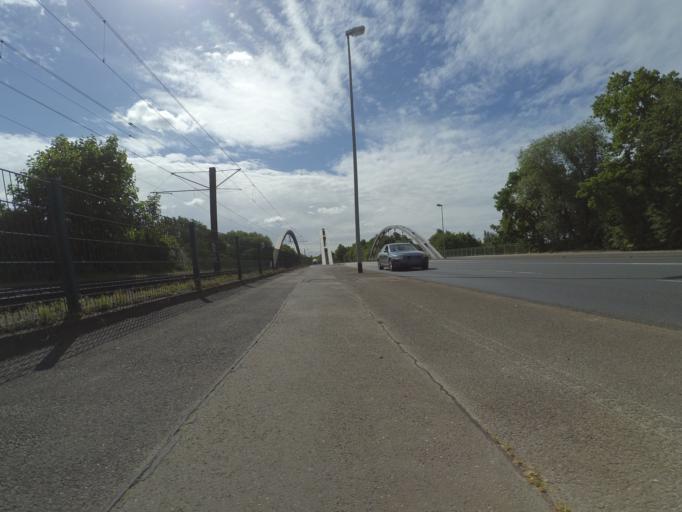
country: DE
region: Lower Saxony
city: Auf der Horst
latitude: 52.4165
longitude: 9.6181
